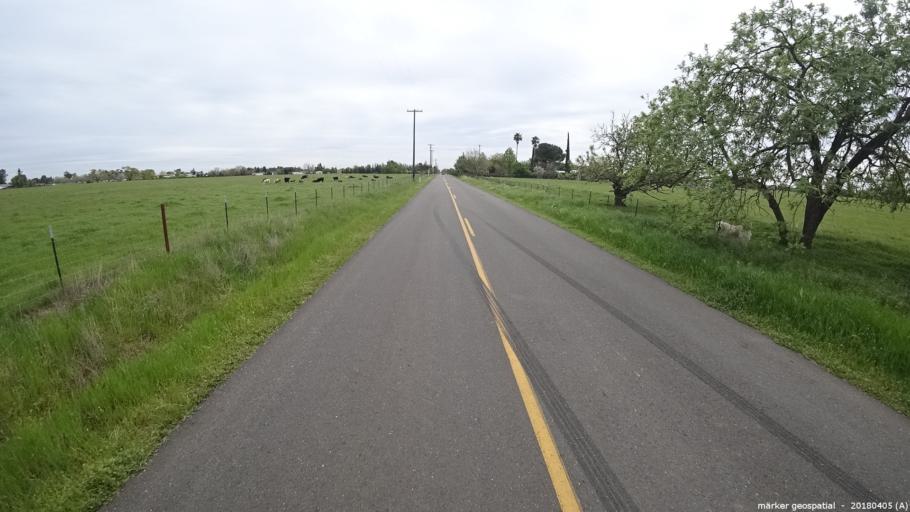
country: US
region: California
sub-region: Sacramento County
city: Galt
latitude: 38.2836
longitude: -121.3369
